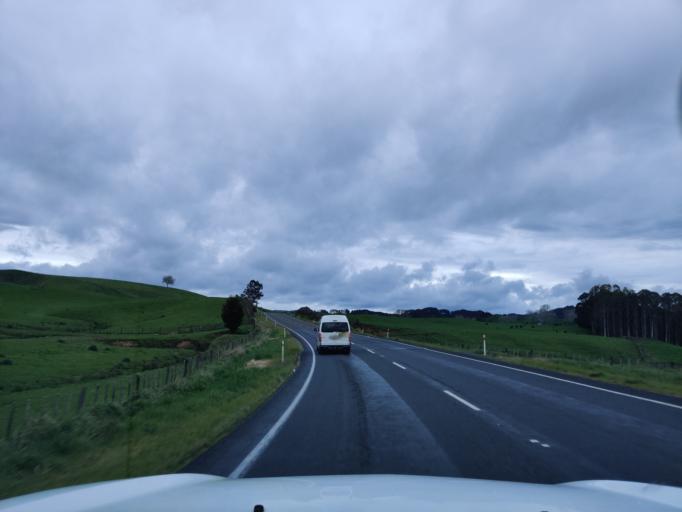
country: NZ
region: Waikato
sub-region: Otorohanga District
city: Otorohanga
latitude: -38.4563
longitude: 175.1672
